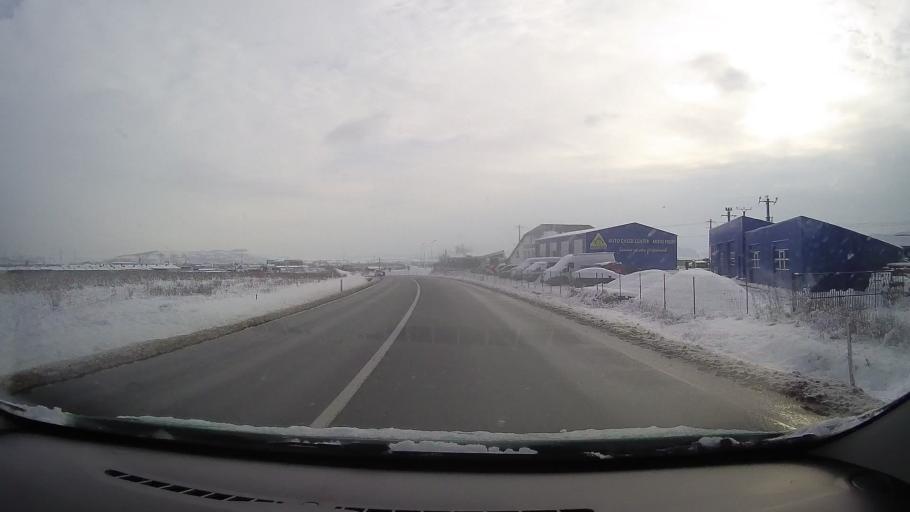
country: RO
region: Alba
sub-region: Municipiul Sebes
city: Lancram
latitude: 45.9611
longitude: 23.5358
